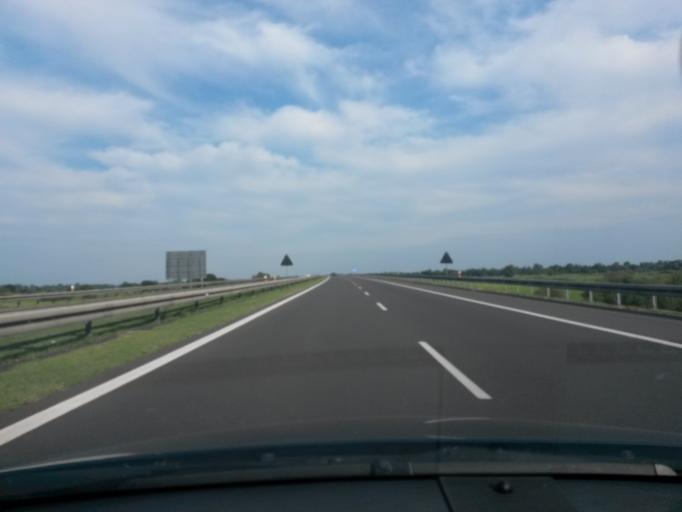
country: PL
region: Greater Poland Voivodeship
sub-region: Powiat koninski
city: Rzgow Pierwszy
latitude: 52.1979
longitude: 18.0433
